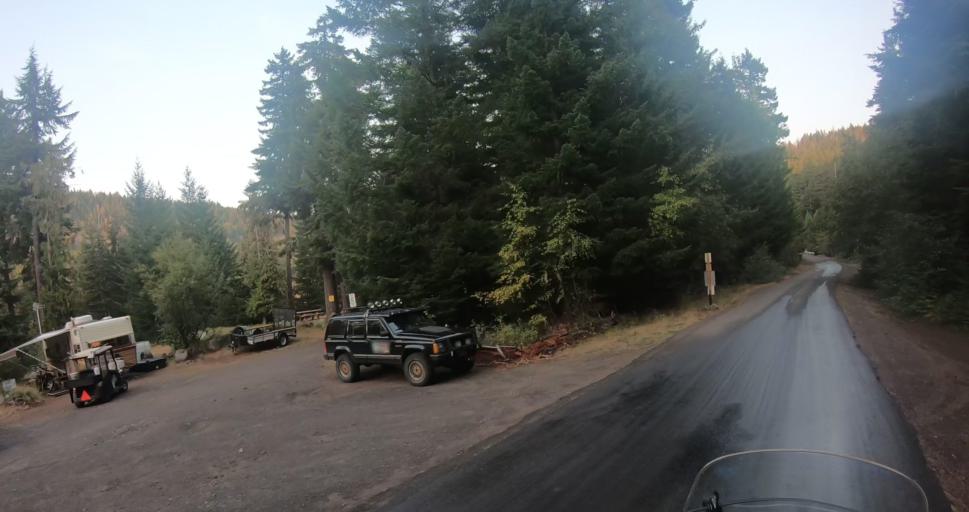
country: US
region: Oregon
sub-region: Hood River County
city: Odell
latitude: 45.4573
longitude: -121.6632
